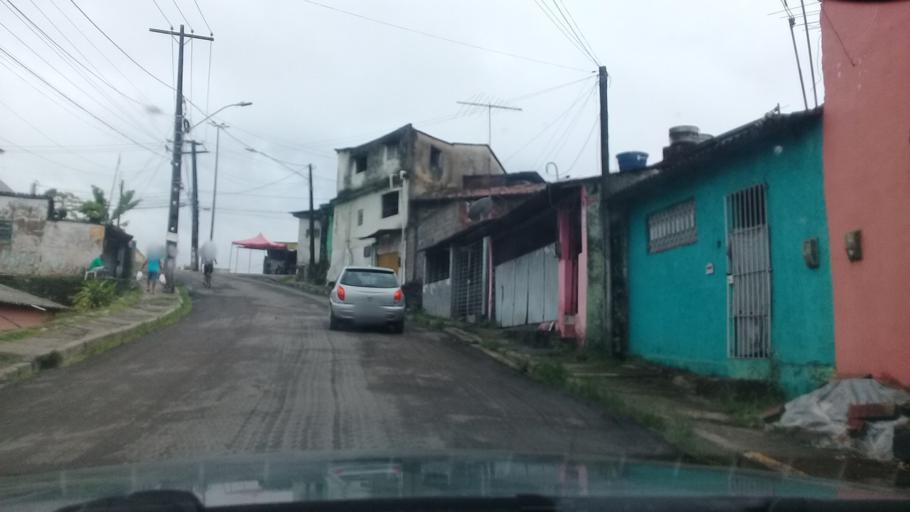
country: BR
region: Pernambuco
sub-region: Jaboatao Dos Guararapes
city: Jaboatao dos Guararapes
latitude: -8.0886
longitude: -34.9738
